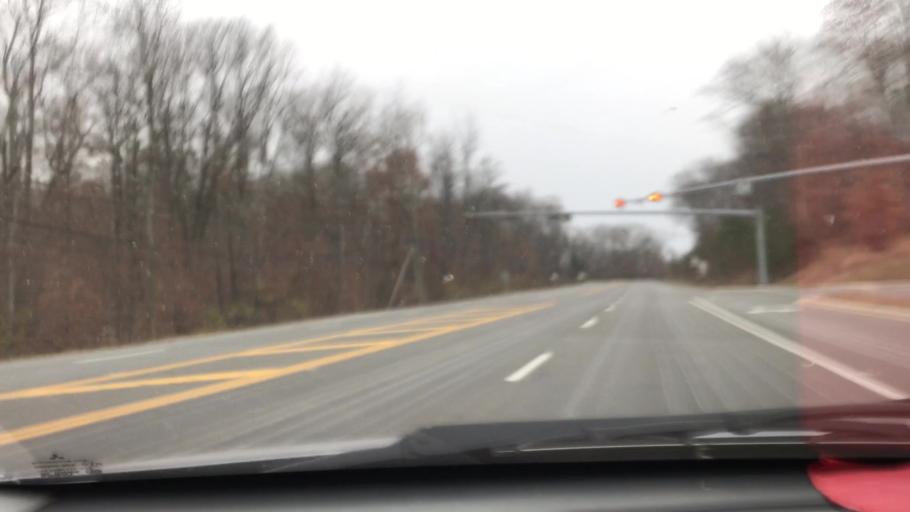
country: US
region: Virginia
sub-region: Prince William County
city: Triangle
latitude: 38.5435
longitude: -77.3382
